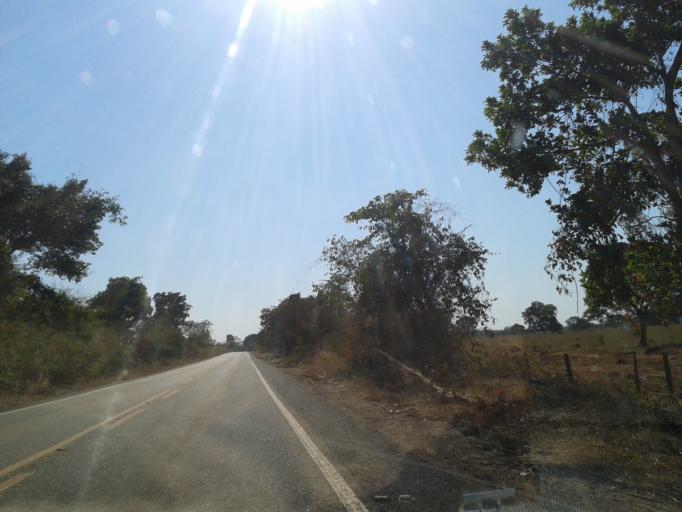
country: BR
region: Goias
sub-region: Mozarlandia
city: Mozarlandia
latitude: -14.6569
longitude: -50.5267
